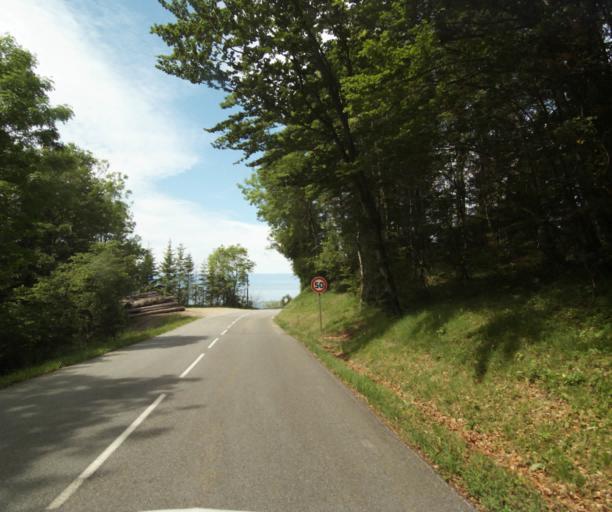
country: FR
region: Rhone-Alpes
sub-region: Departement de la Haute-Savoie
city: Perrignier
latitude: 46.2723
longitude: 6.4520
